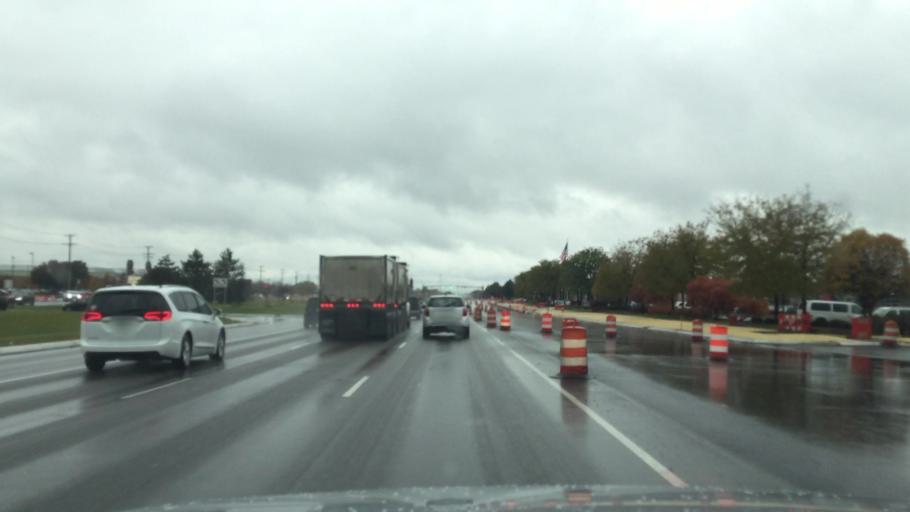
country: US
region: Michigan
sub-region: Macomb County
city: Clinton
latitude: 42.6285
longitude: -82.9381
